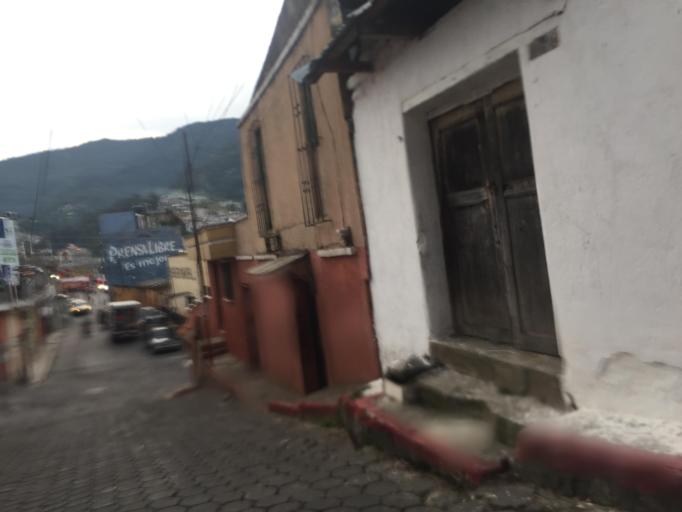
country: GT
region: Totonicapan
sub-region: Municipio de Totonicapan
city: Totonicapan
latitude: 14.9091
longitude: -91.3619
